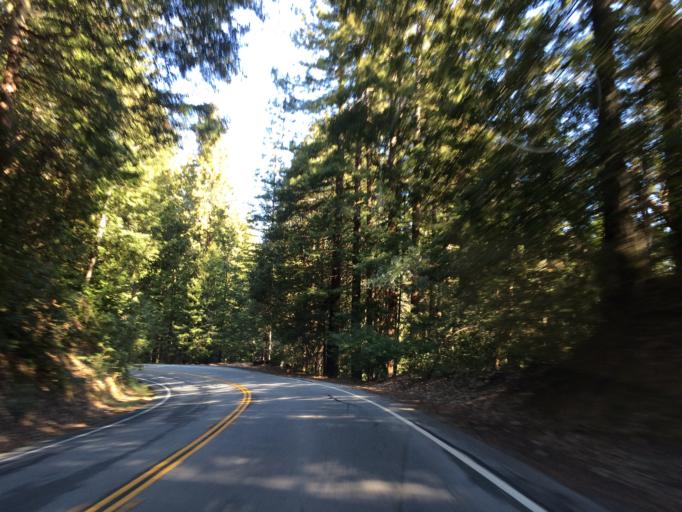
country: US
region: California
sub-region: Santa Cruz County
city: Boulder Creek
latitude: 37.2191
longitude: -122.1526
